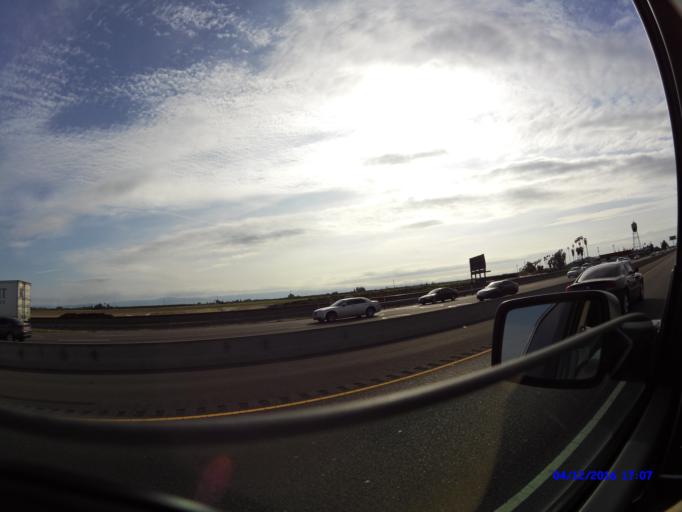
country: US
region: California
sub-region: San Joaquin County
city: Ripon
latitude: 37.7629
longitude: -121.1606
